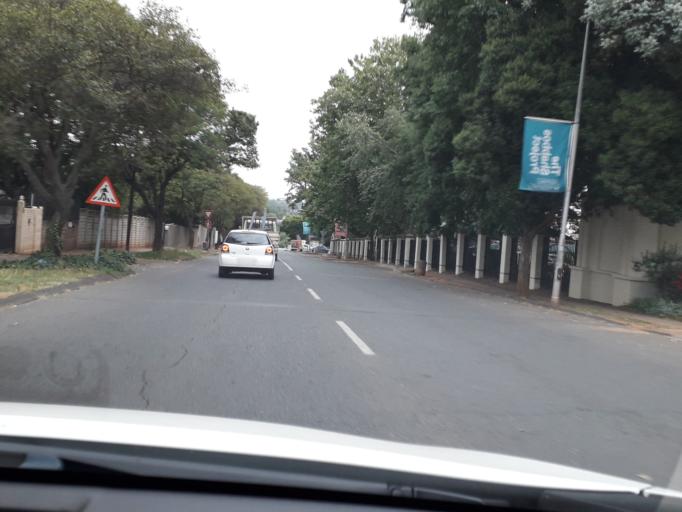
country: ZA
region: Gauteng
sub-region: City of Johannesburg Metropolitan Municipality
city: Johannesburg
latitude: -26.1418
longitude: 28.0782
